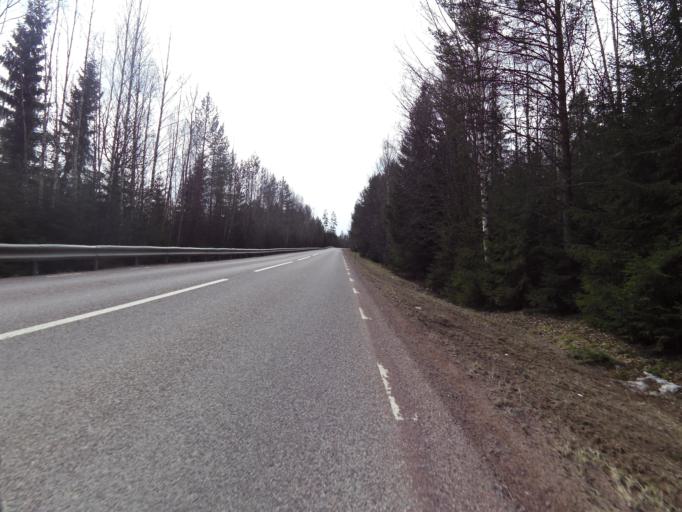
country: SE
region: Dalarna
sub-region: Hedemora Kommun
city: Langshyttan
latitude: 60.5389
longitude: 16.1306
